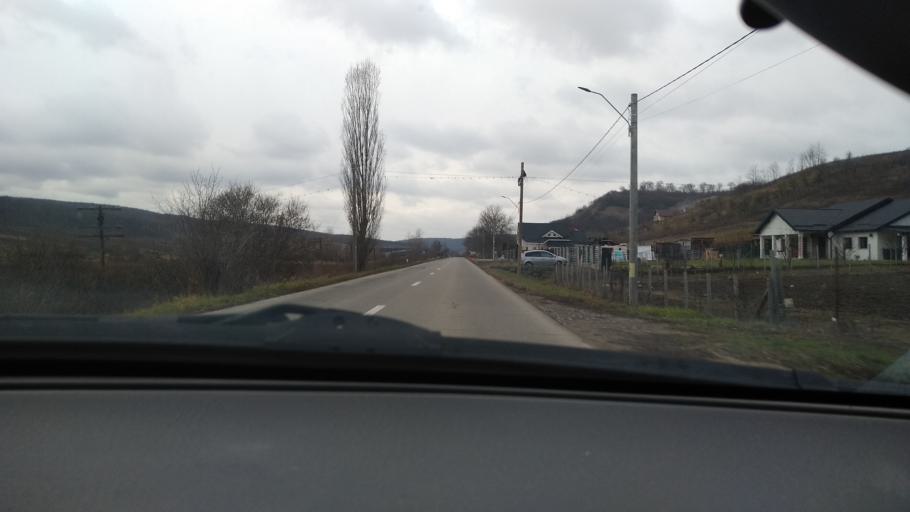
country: RO
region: Mures
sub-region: Comuna Livezeni
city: Livezeni
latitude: 46.5444
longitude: 24.6610
